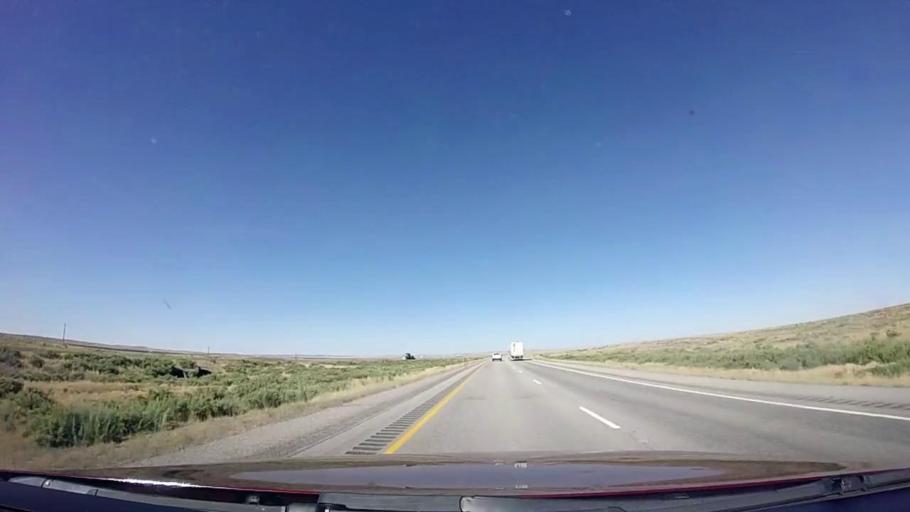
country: US
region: Wyoming
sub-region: Carbon County
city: Rawlins
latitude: 41.7864
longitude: -107.4047
